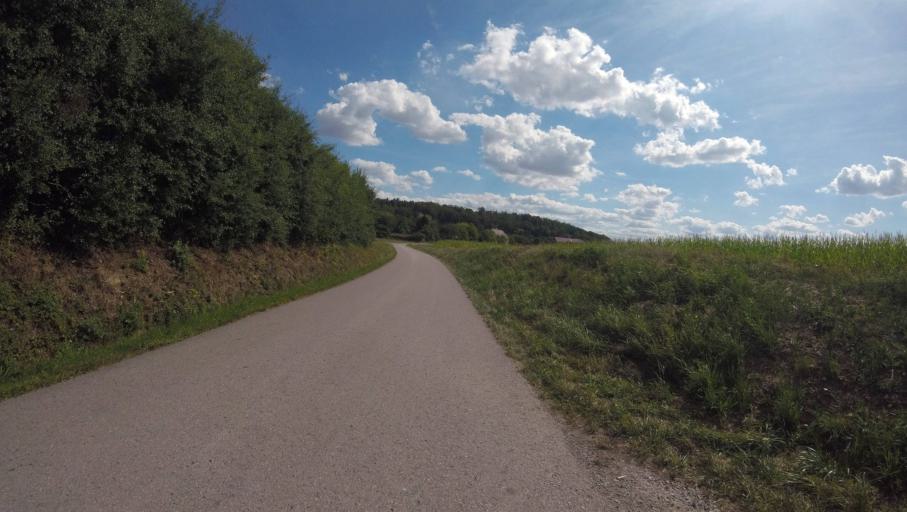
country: DE
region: Baden-Wuerttemberg
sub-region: Regierungsbezirk Stuttgart
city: Aspach
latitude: 48.9867
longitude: 9.3799
